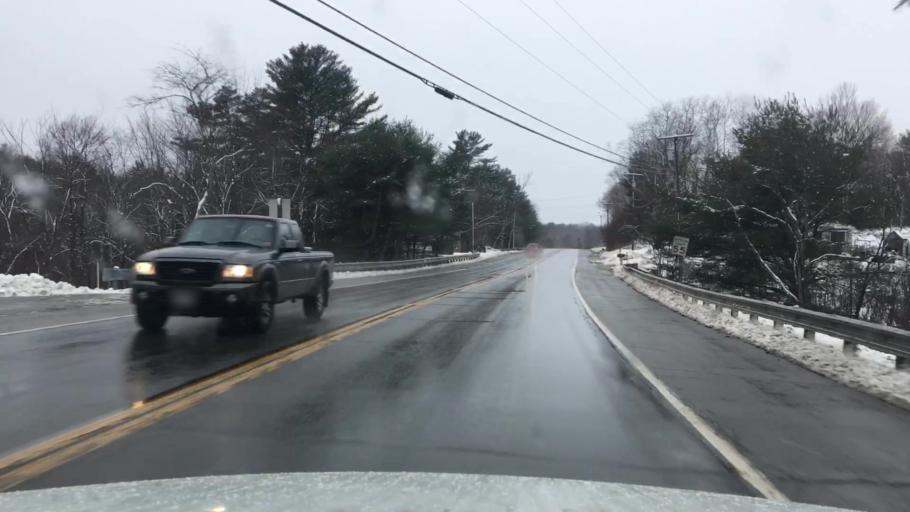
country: US
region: Maine
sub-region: Knox County
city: Rockport
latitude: 44.1801
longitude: -69.1394
